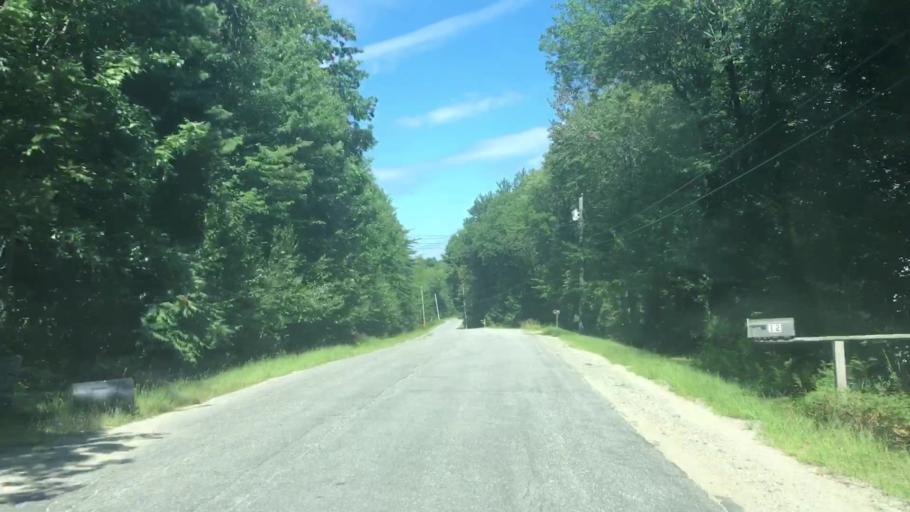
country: US
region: Maine
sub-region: Androscoggin County
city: Sabattus
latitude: 44.1188
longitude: -70.0255
